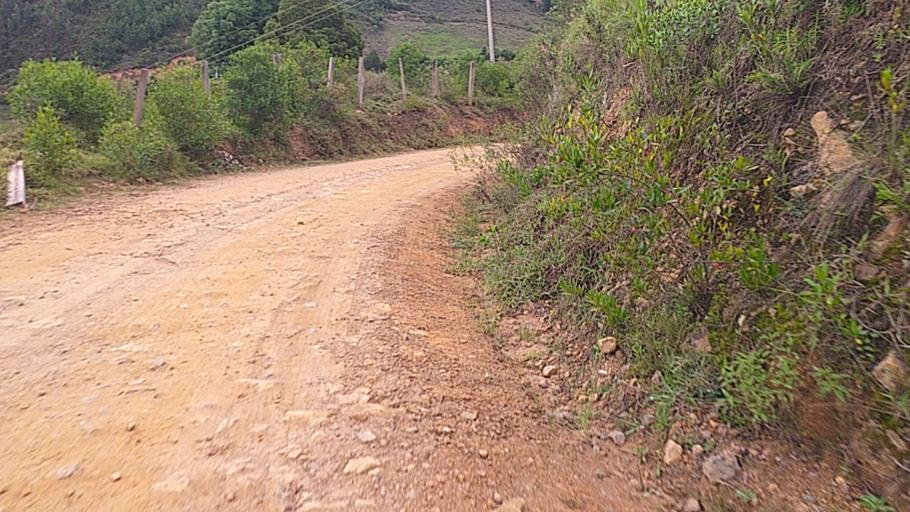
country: CO
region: Boyaca
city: Floresta
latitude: 5.8755
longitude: -72.9151
